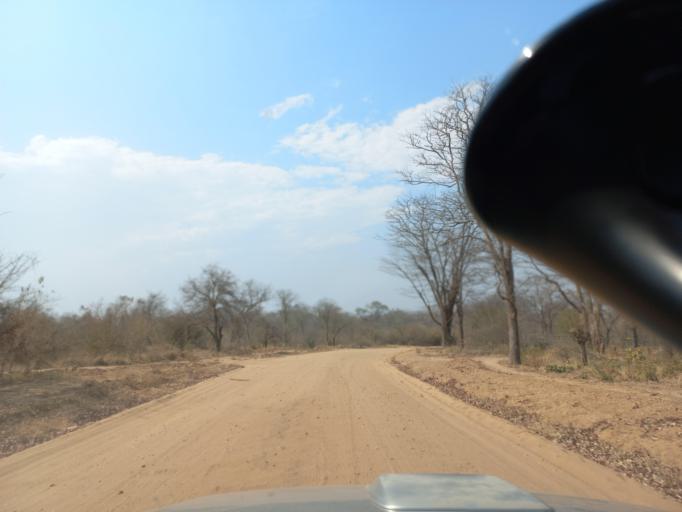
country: ZW
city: Chirundu
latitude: -15.9317
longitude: 28.9156
